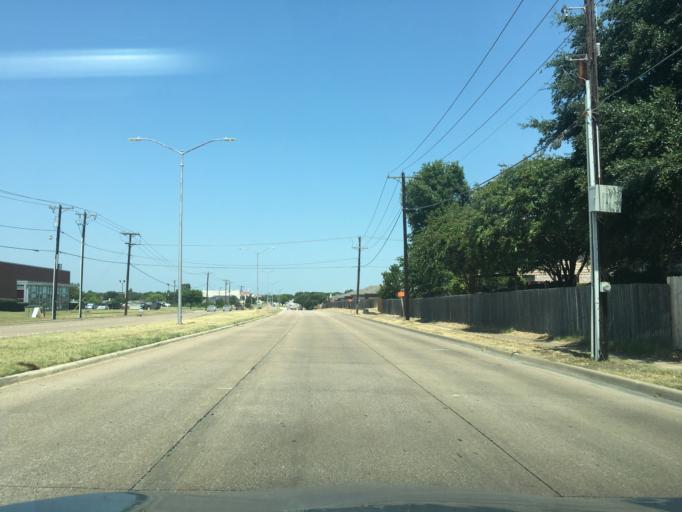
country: US
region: Texas
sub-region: Tarrant County
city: Crowley
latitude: 32.6220
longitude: -97.3698
